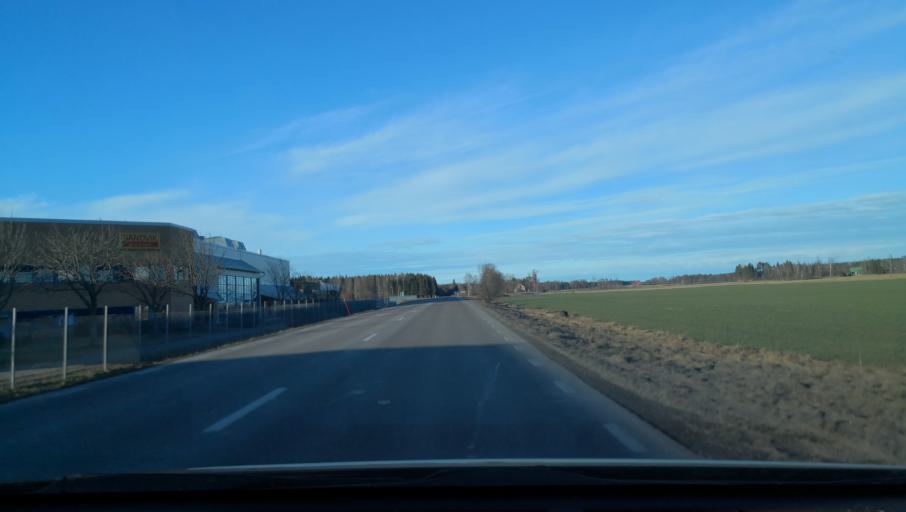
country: SE
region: Uppsala
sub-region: Osthammars Kommun
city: Gimo
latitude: 60.1800
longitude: 18.1905
